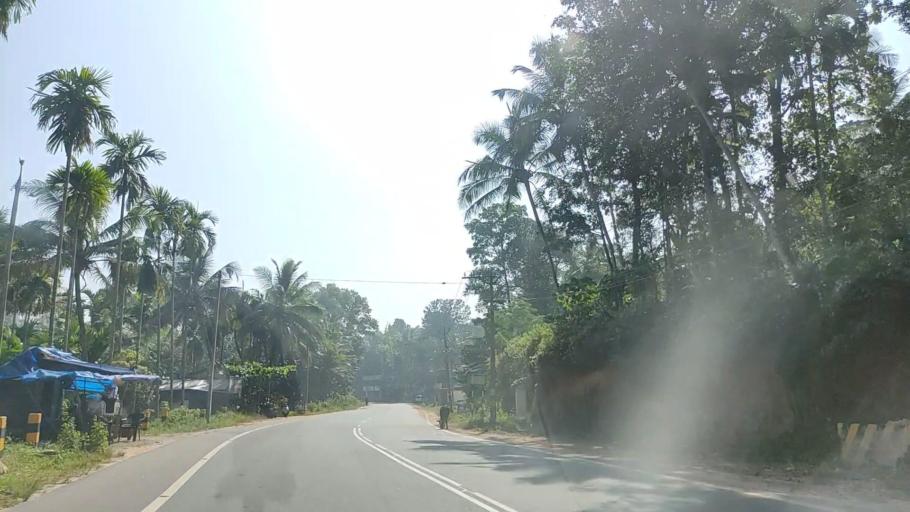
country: IN
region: Kerala
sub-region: Kollam
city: Punalur
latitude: 8.9325
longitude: 76.9636
